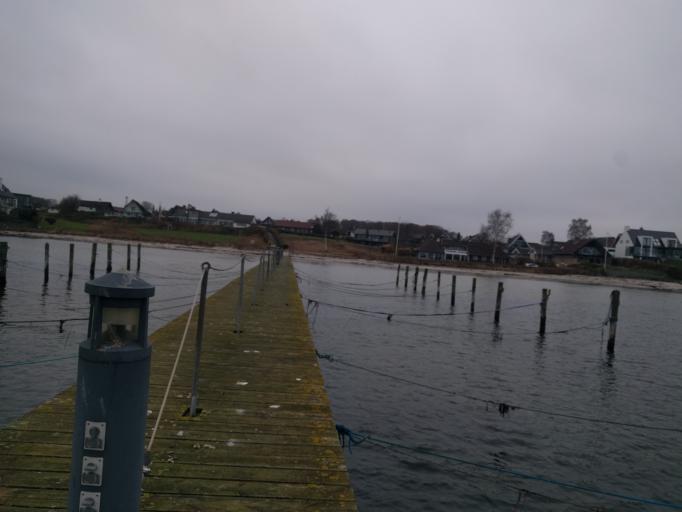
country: DK
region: South Denmark
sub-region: Fredericia Kommune
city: Snoghoj
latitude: 55.5418
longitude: 9.7323
